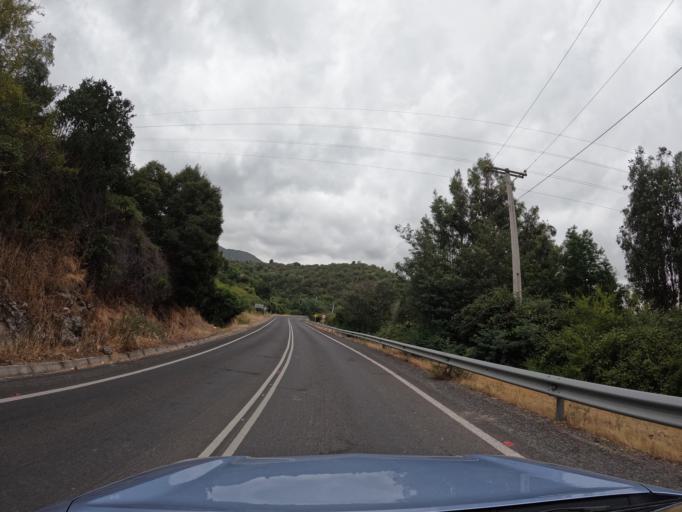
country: CL
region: O'Higgins
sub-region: Provincia de Colchagua
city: Chimbarongo
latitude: -34.7281
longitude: -71.0945
